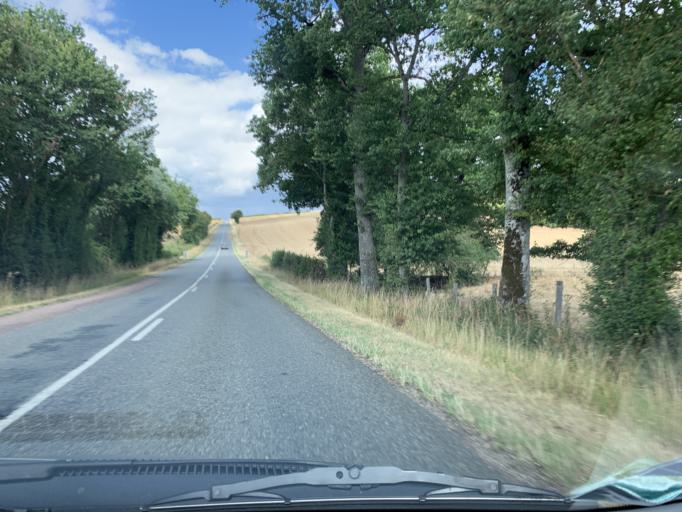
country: FR
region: Bourgogne
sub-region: Departement de la Nievre
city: Varzy
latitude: 47.4033
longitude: 3.4499
